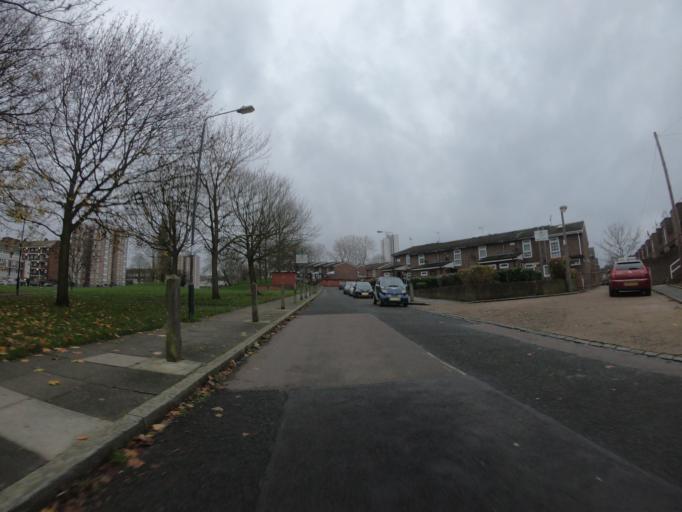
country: GB
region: England
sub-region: Greater London
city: Woolwich
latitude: 51.4892
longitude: 0.0780
